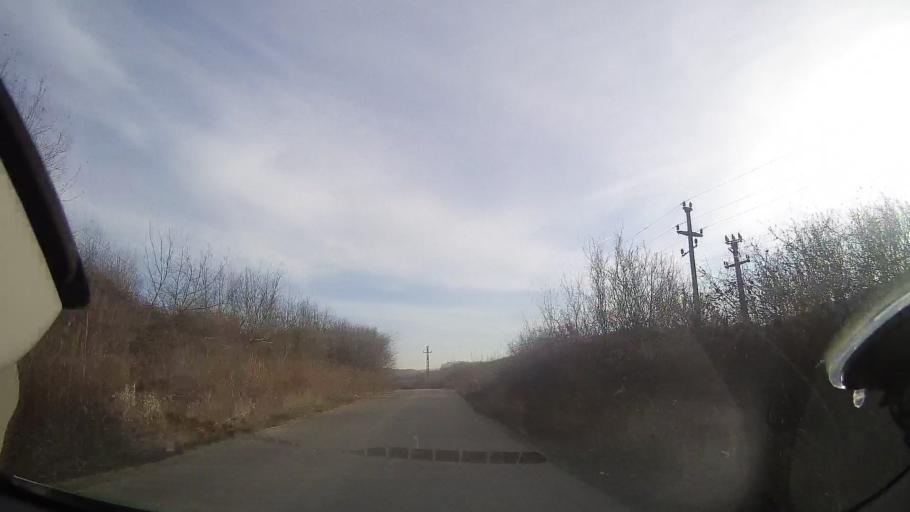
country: RO
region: Bihor
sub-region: Comuna Sarbi
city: Sarbi
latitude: 47.1806
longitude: 22.1360
